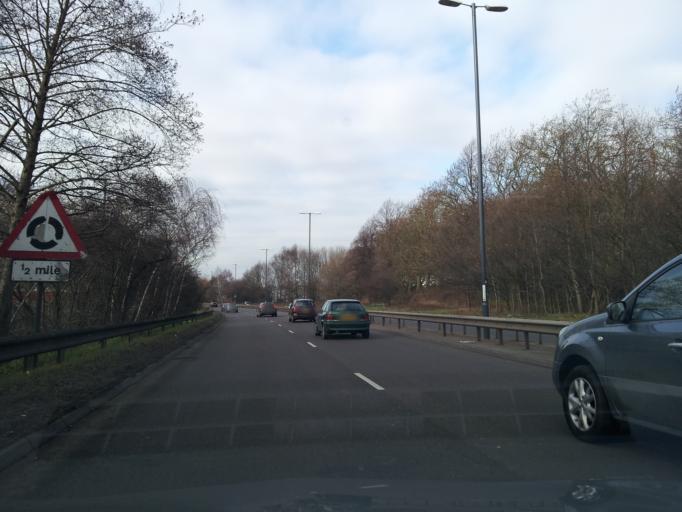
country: GB
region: England
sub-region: Derby
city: Derby
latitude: 52.9216
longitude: -1.4493
